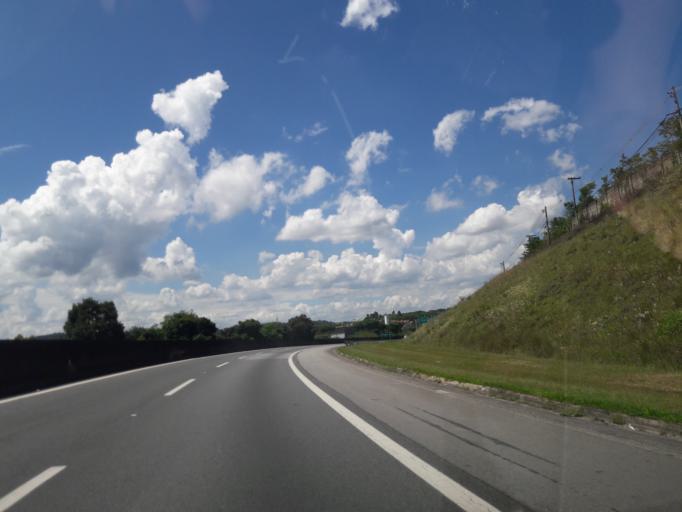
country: BR
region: Sao Paulo
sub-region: Cajamar
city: Cajamar
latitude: -23.3469
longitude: -46.8447
